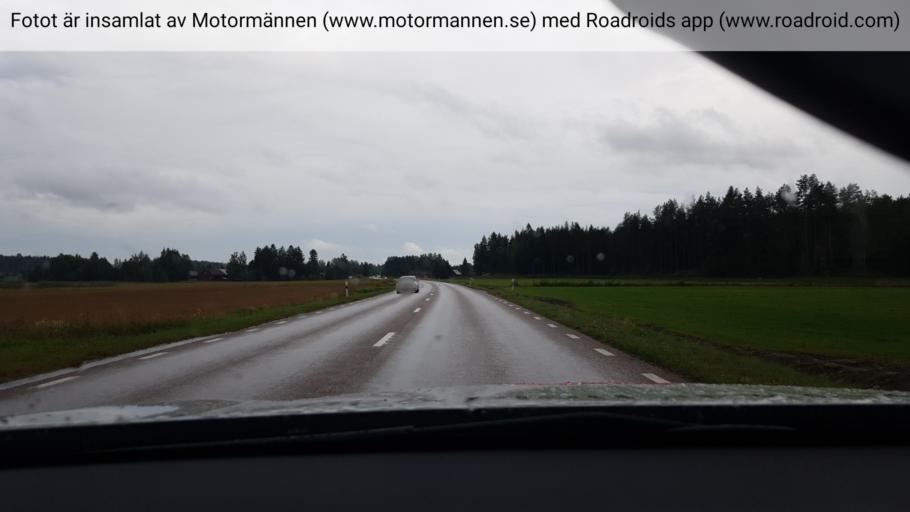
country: SE
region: Uppsala
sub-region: Tierps Kommun
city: Karlholmsbruk
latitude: 60.4486
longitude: 17.7722
